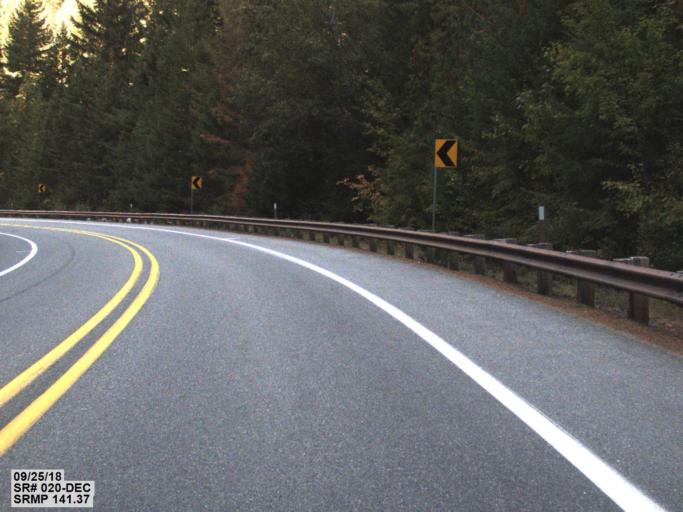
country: US
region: Washington
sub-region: Snohomish County
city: Darrington
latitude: 48.7056
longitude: -120.9148
